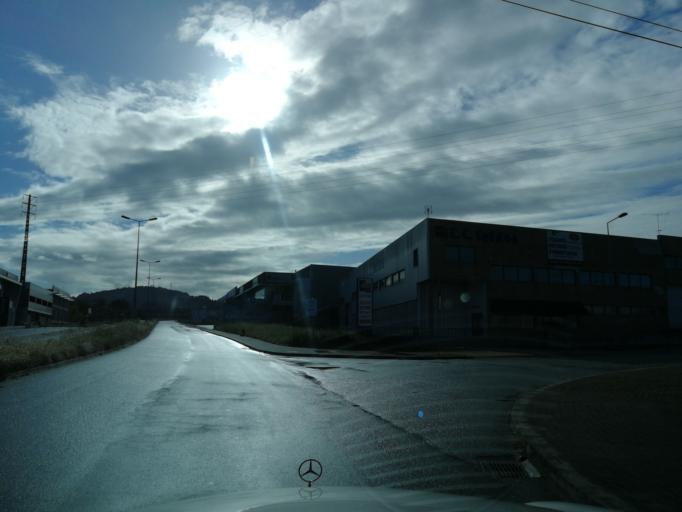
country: PT
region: Braga
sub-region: Braga
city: Braga
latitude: 41.5656
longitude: -8.4450
